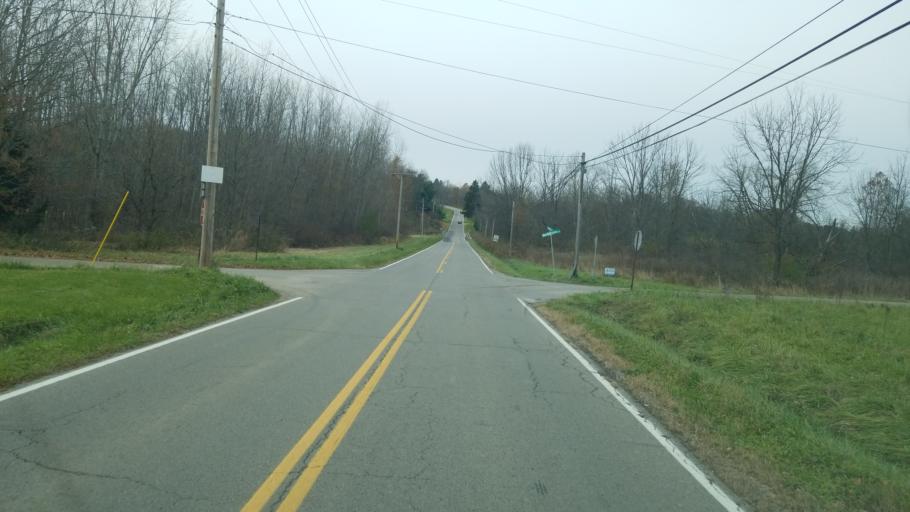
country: US
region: Ohio
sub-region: Richland County
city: Lincoln Heights
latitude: 40.7285
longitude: -82.4814
